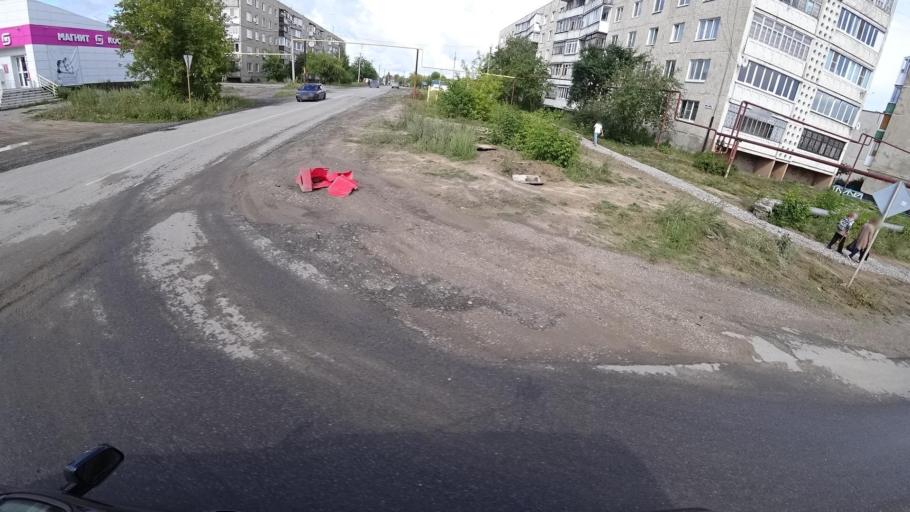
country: RU
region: Sverdlovsk
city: Kamyshlov
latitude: 56.8366
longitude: 62.7297
